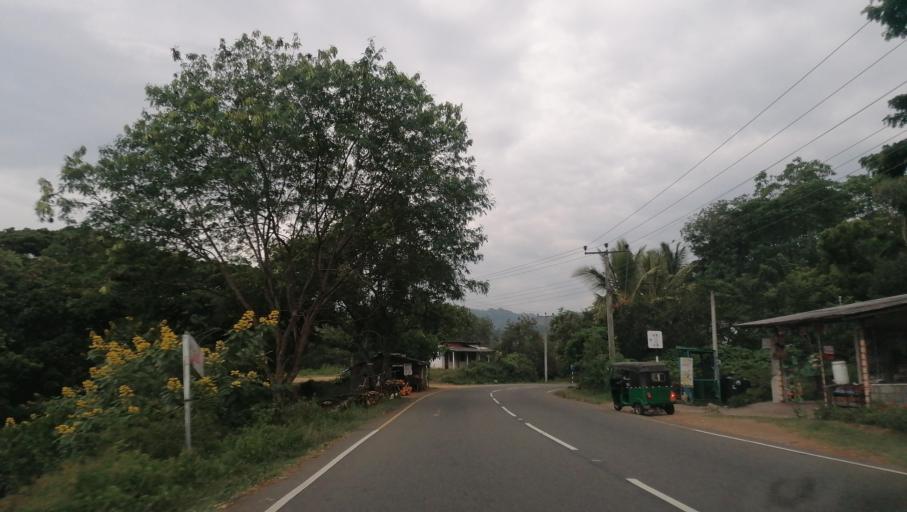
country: LK
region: Central
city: Kandy
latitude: 7.2228
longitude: 80.7637
